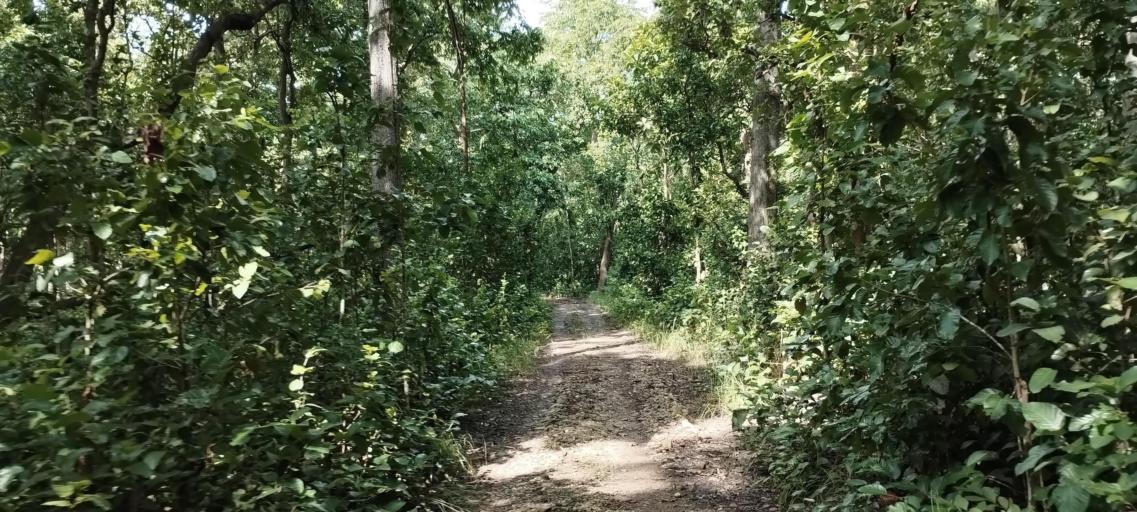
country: NP
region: Far Western
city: Tikapur
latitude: 28.5529
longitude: 81.2912
